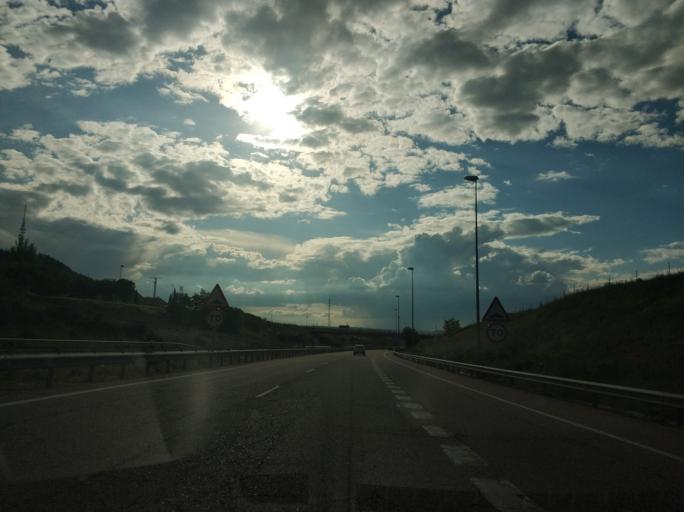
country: ES
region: Castille and Leon
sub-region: Provincia de Valladolid
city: Cisterniga
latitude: 41.6169
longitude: -4.6859
